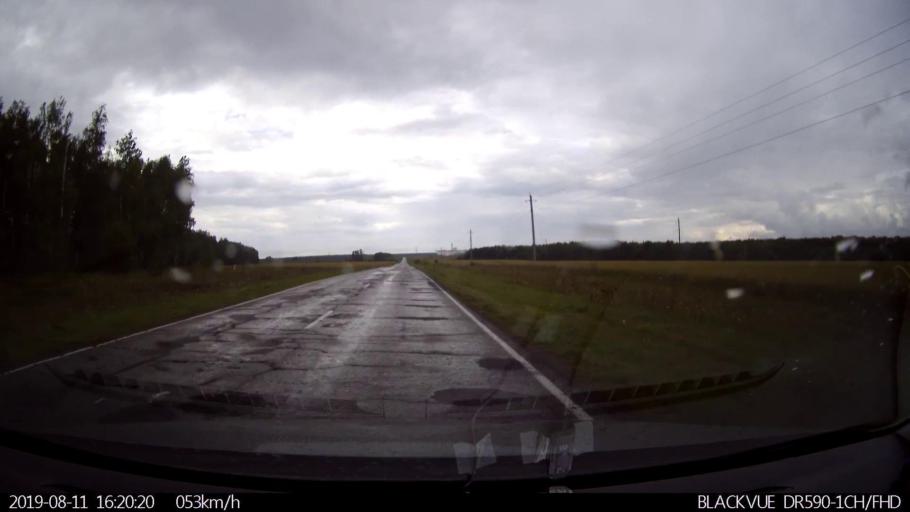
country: RU
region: Ulyanovsk
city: Mayna
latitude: 54.0709
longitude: 47.6034
